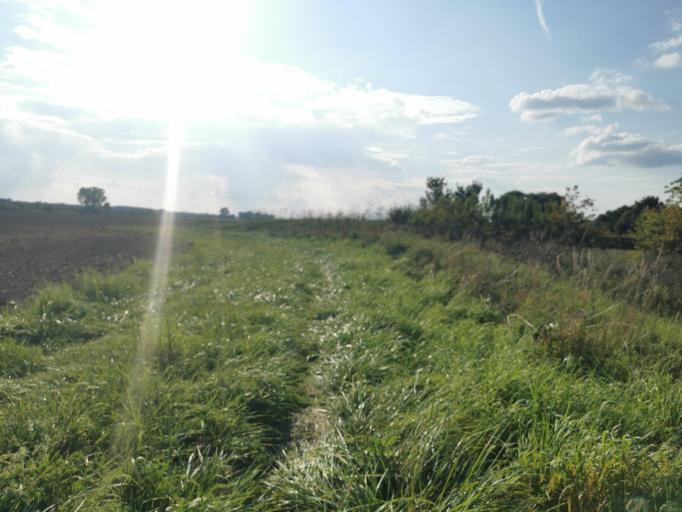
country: SK
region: Trnavsky
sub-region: Okres Senica
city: Senica
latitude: 48.6671
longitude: 17.2953
